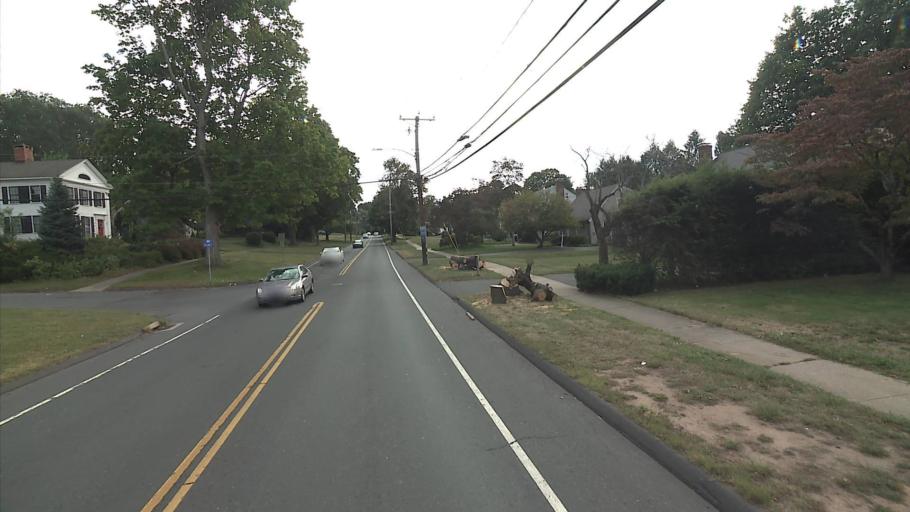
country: US
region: Connecticut
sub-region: Hartford County
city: Newington
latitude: 41.6893
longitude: -72.7217
